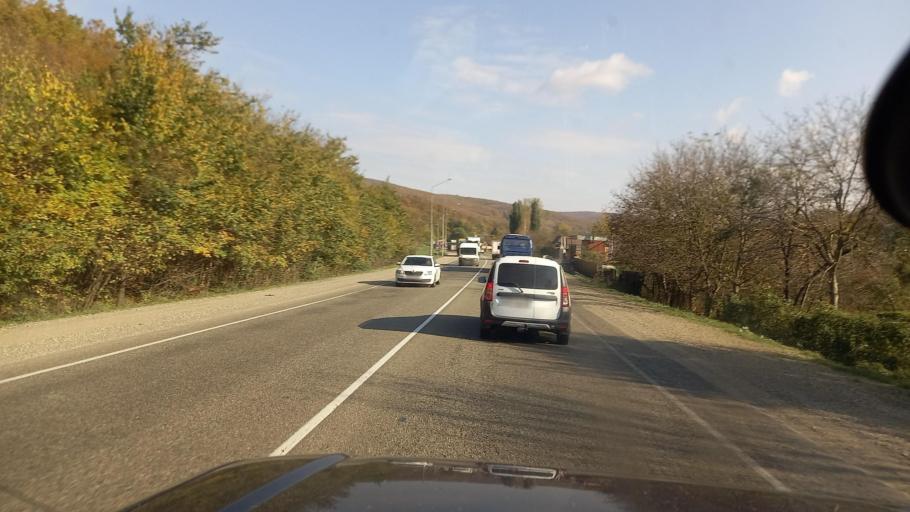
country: RU
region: Krasnodarskiy
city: Verkhnebakanskiy
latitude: 44.8584
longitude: 37.7346
